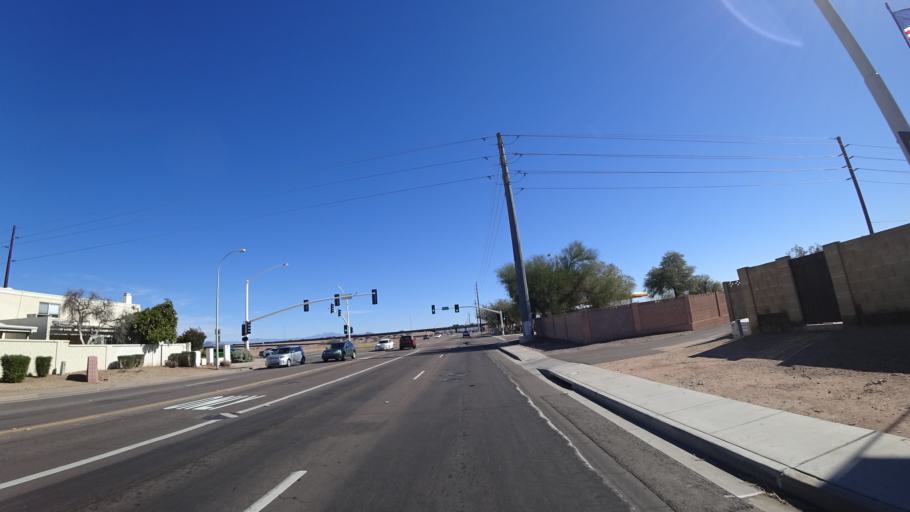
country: US
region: Arizona
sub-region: Maricopa County
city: Scottsdale
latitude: 33.4948
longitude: -111.8925
